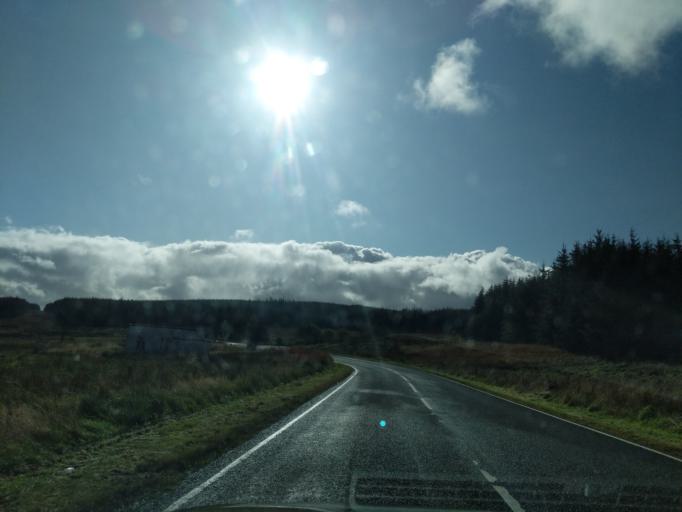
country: GB
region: Scotland
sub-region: Dumfries and Galloway
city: Moffat
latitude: 55.3878
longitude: -3.4859
